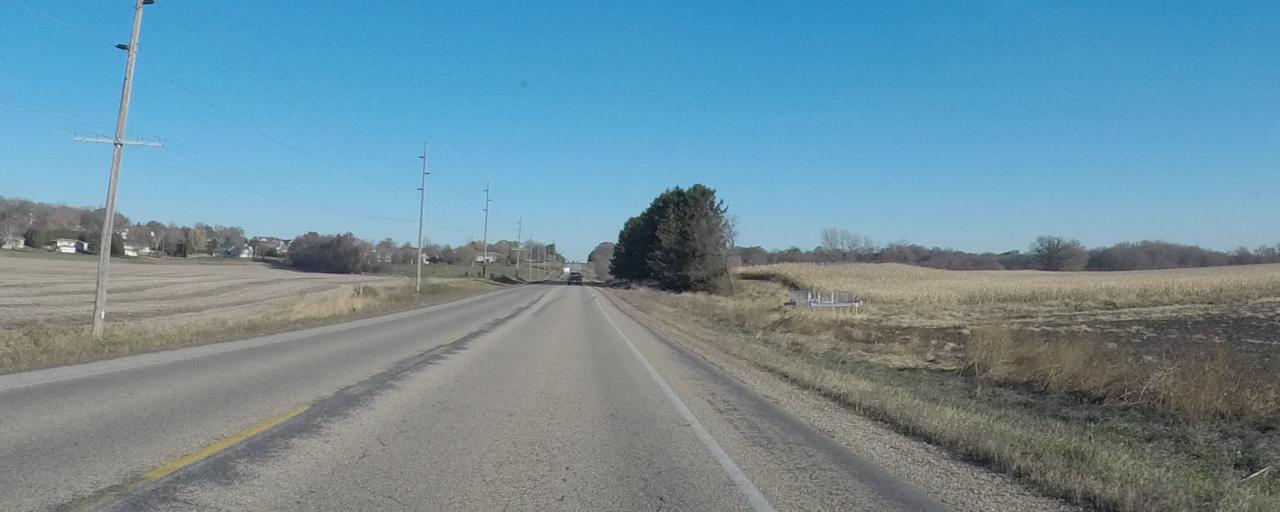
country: US
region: Wisconsin
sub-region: Dane County
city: Cottage Grove
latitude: 43.0422
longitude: -89.1999
